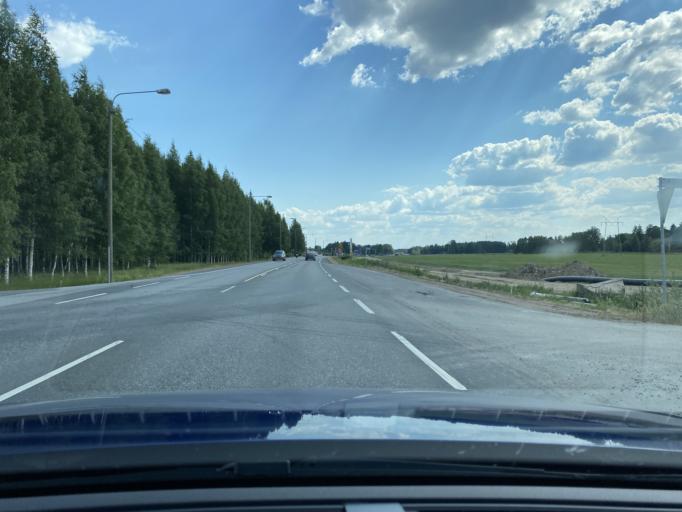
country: FI
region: Satakunta
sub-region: Rauma
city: Eura
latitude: 61.1369
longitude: 22.1197
